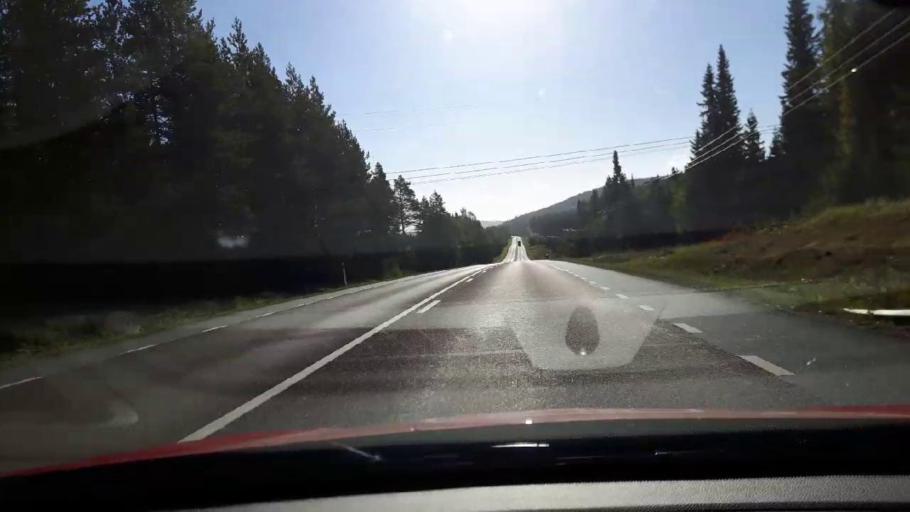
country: SE
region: Jaemtland
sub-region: Braecke Kommun
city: Braecke
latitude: 62.9452
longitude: 15.1720
